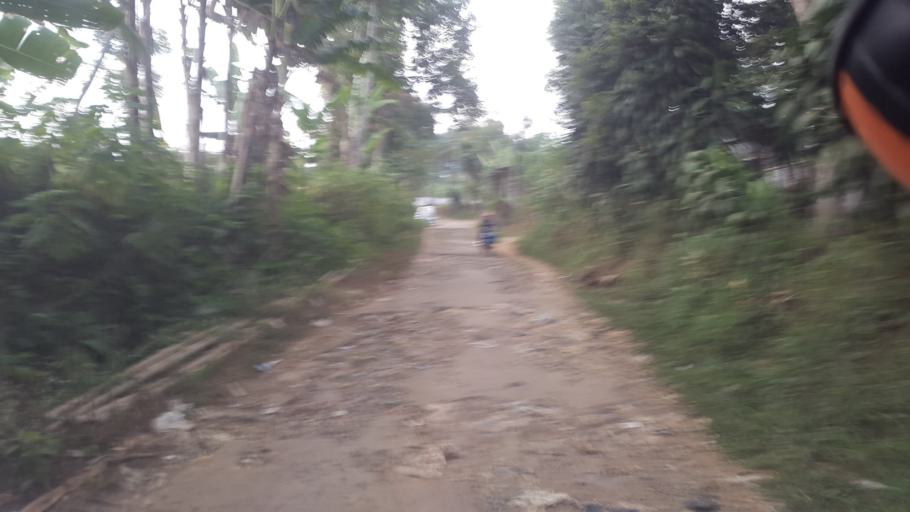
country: ID
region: West Java
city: Sukabumi
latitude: -6.8838
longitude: 106.9585
